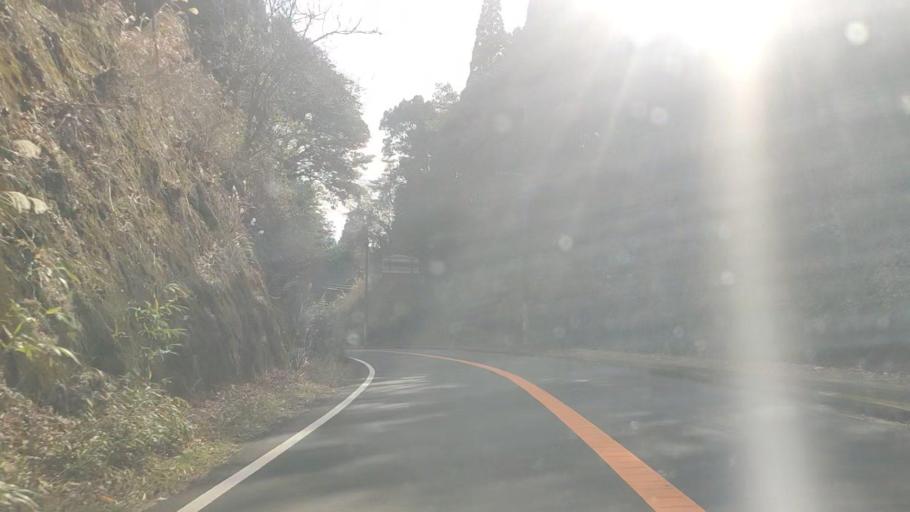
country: JP
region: Kagoshima
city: Kajiki
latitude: 31.8273
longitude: 130.6889
